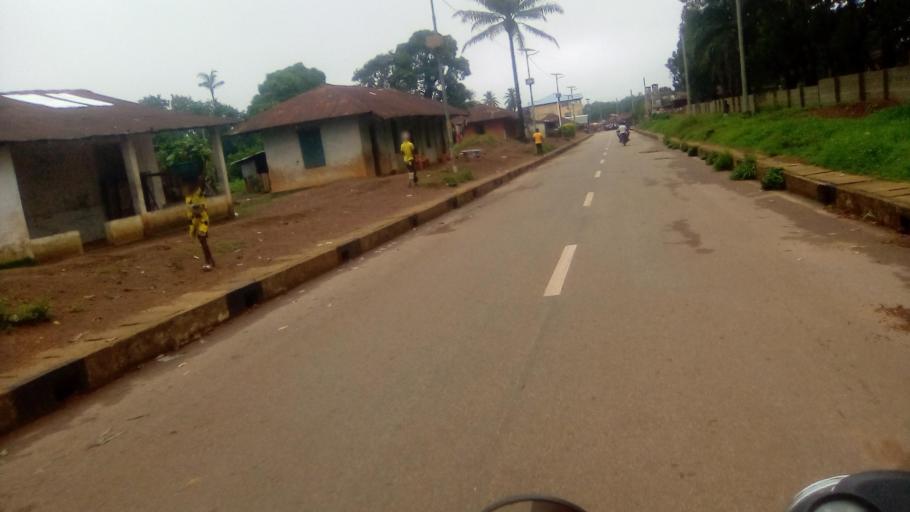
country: SL
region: Southern Province
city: Moyamba
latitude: 8.1543
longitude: -12.4308
